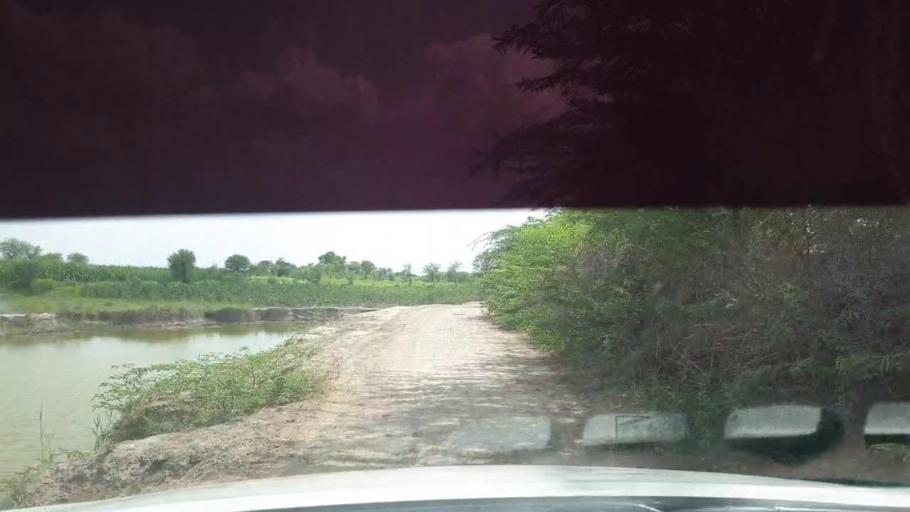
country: PK
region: Sindh
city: Kadhan
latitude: 24.6188
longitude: 69.0303
